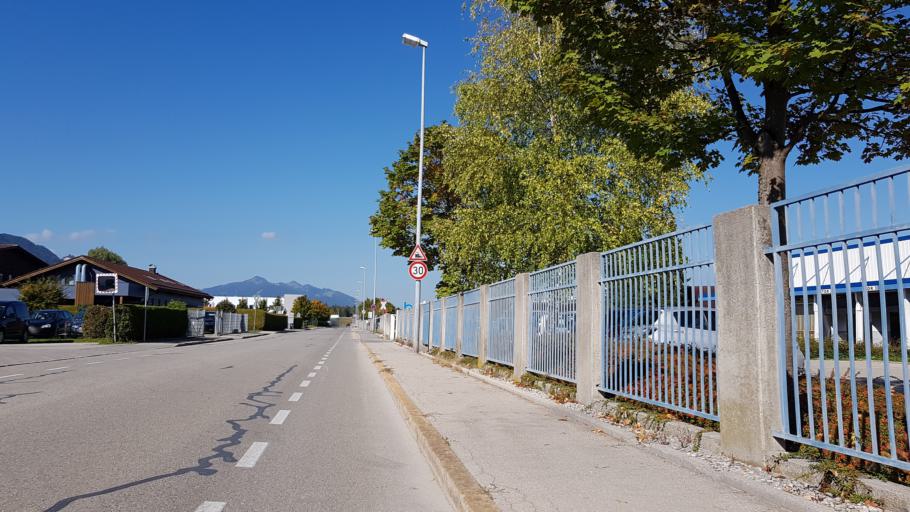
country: DE
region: Bavaria
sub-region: Swabia
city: Fuessen
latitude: 47.5732
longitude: 10.6724
